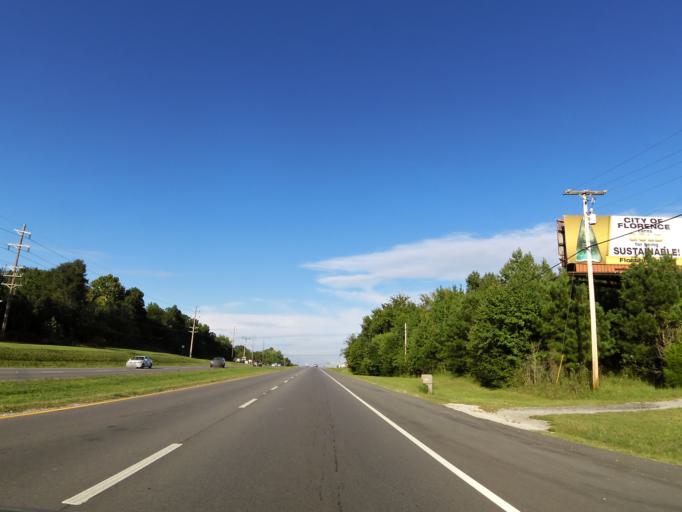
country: US
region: Alabama
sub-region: Lauderdale County
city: Killen
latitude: 34.8426
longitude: -87.5899
